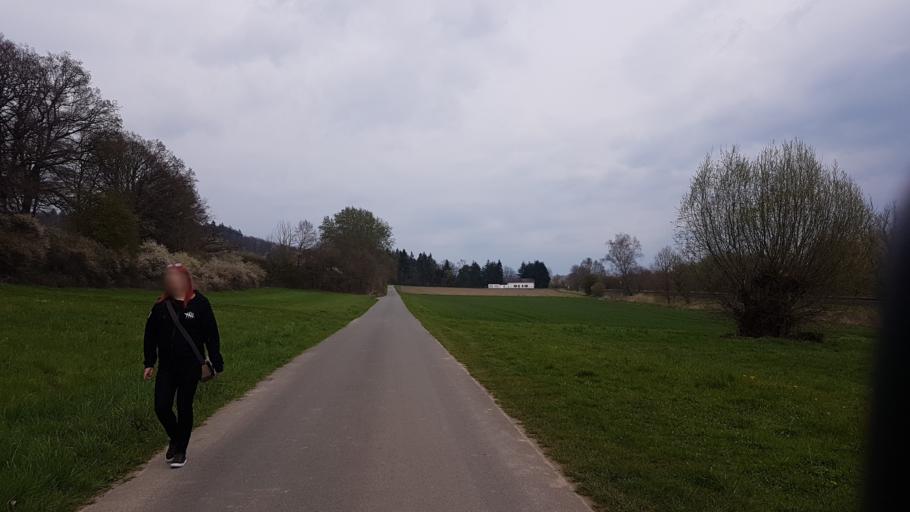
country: DE
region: Lower Saxony
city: Hameln
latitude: 52.1284
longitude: 9.3186
